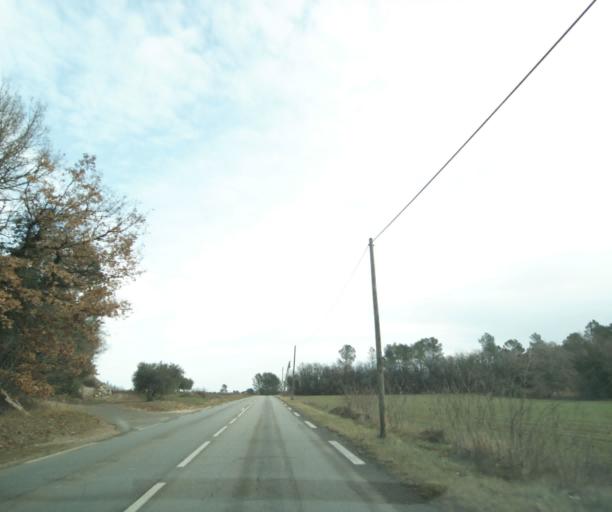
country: FR
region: Provence-Alpes-Cote d'Azur
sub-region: Departement du Var
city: Rougiers
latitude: 43.3978
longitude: 5.8803
